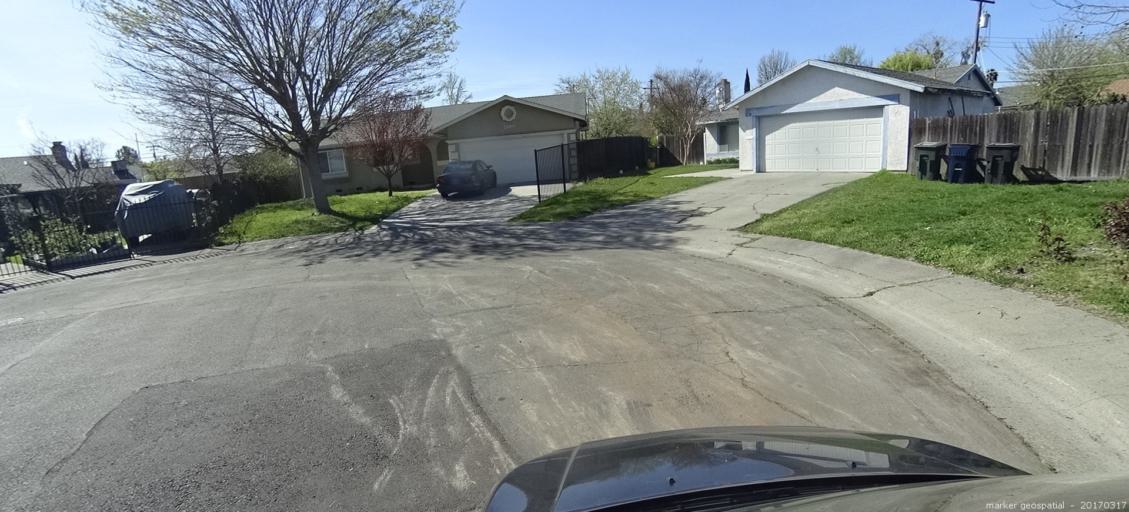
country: US
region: California
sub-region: Sacramento County
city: Parkway
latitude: 38.4866
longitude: -121.4907
